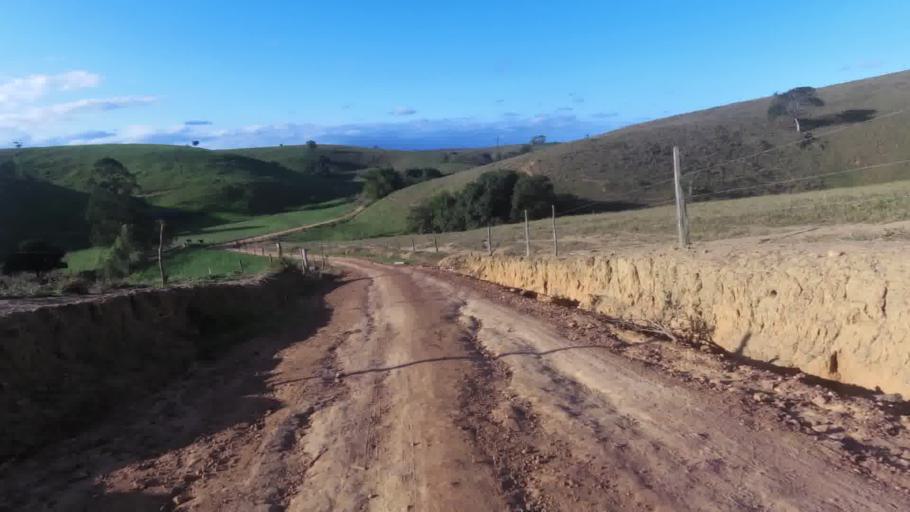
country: BR
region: Espirito Santo
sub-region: Marataizes
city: Marataizes
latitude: -21.1508
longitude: -41.0331
